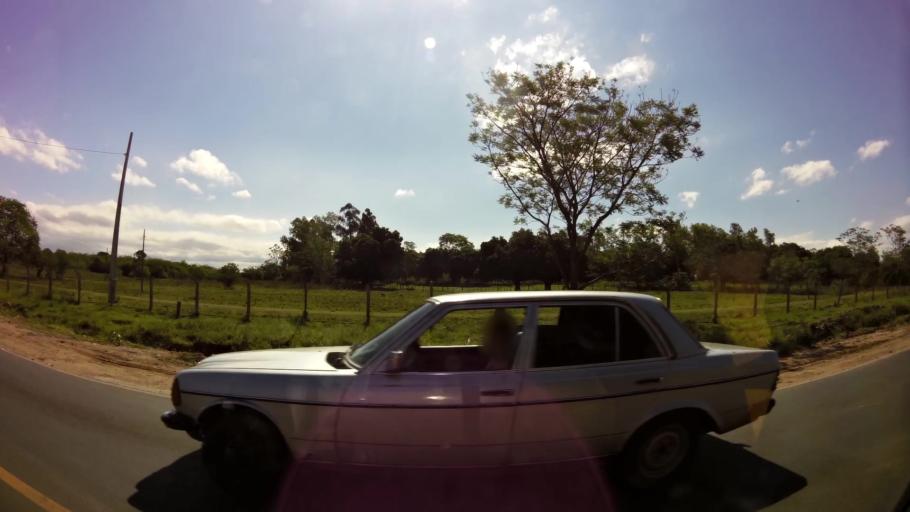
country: PY
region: Central
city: Fernando de la Mora
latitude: -25.2769
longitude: -57.5233
